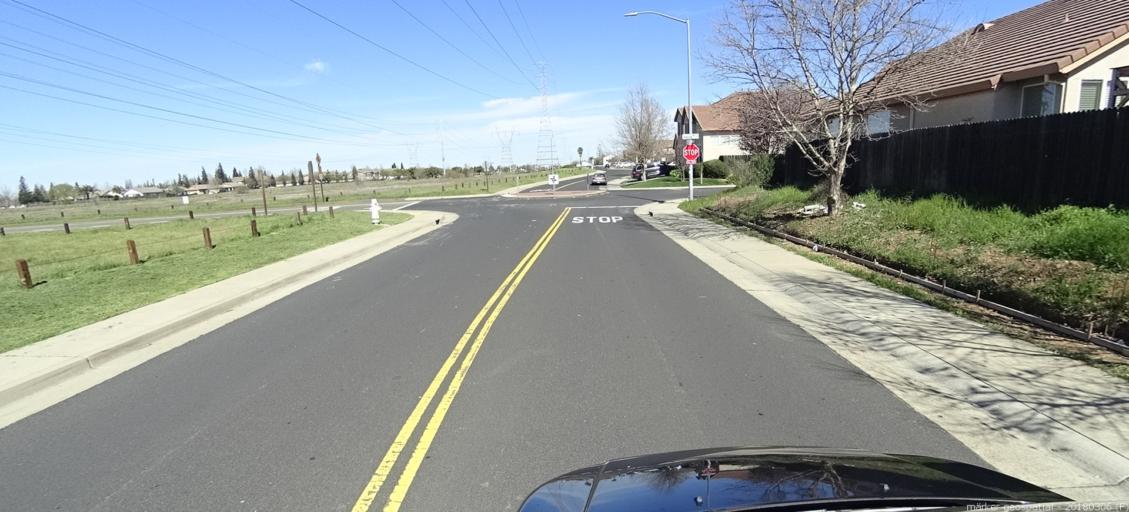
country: US
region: California
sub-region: Sacramento County
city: Vineyard
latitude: 38.4571
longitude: -121.3512
